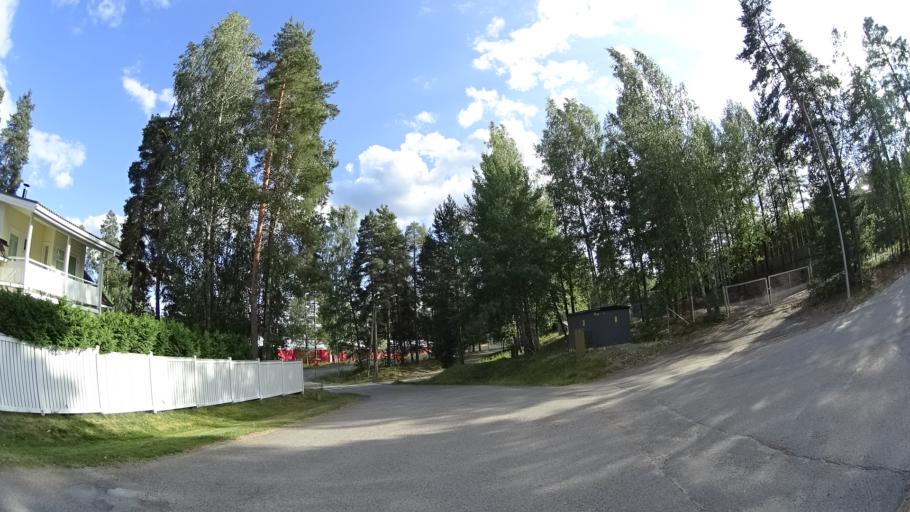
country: FI
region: Uusimaa
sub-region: Helsinki
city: Vihti
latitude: 60.3467
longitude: 24.3284
